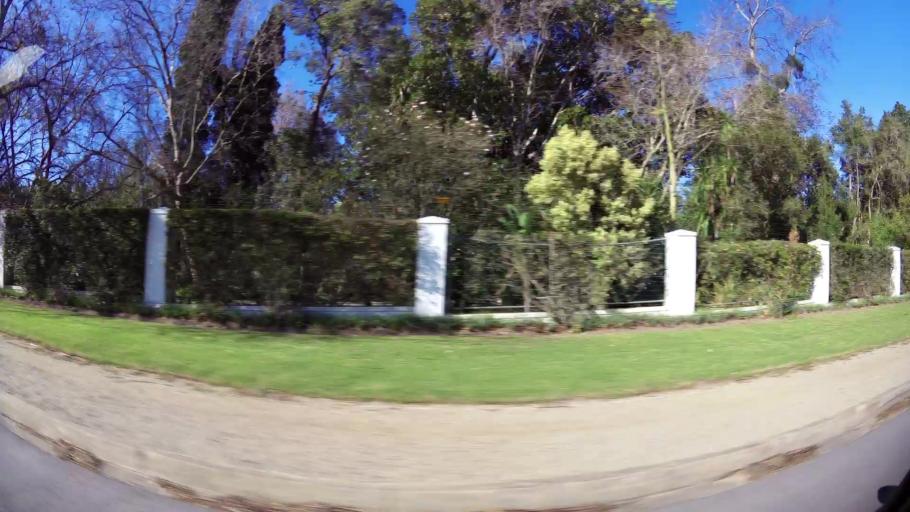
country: ZA
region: Western Cape
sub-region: Eden District Municipality
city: George
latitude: -33.9519
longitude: 22.4051
